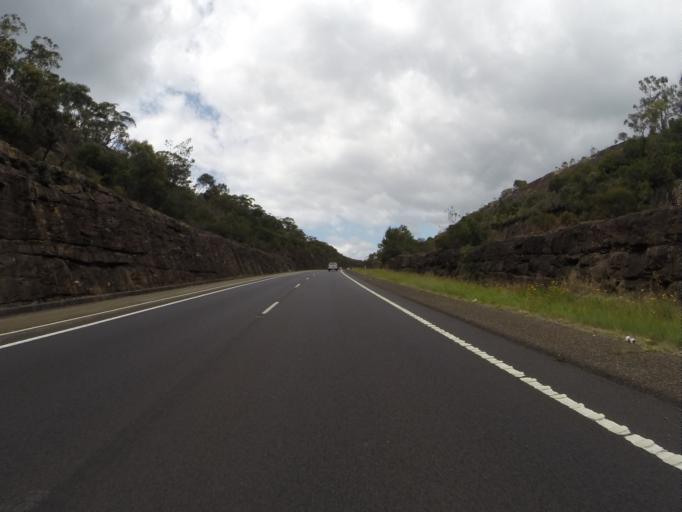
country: AU
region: New South Wales
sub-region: Wollongong
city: Helensburgh
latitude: -34.1712
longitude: 150.9782
